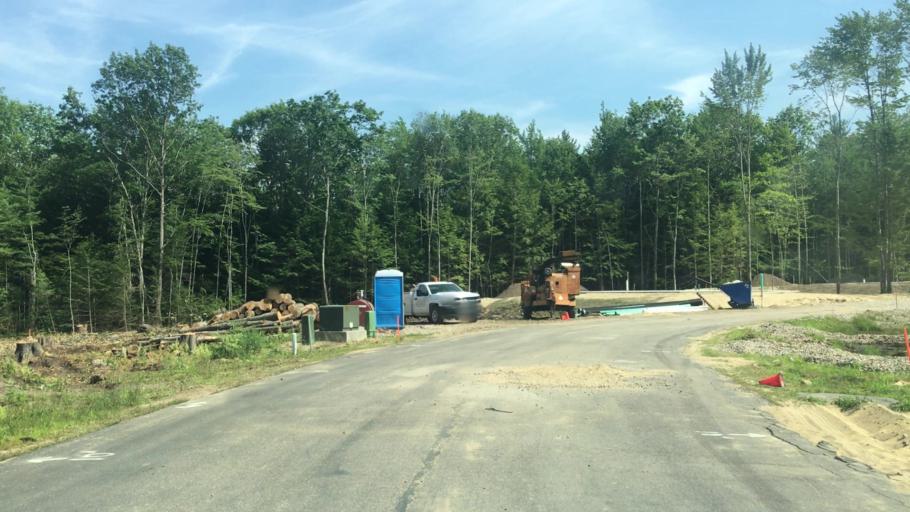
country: US
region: New Hampshire
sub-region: Strafford County
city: Rochester
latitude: 43.3126
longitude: -70.9232
